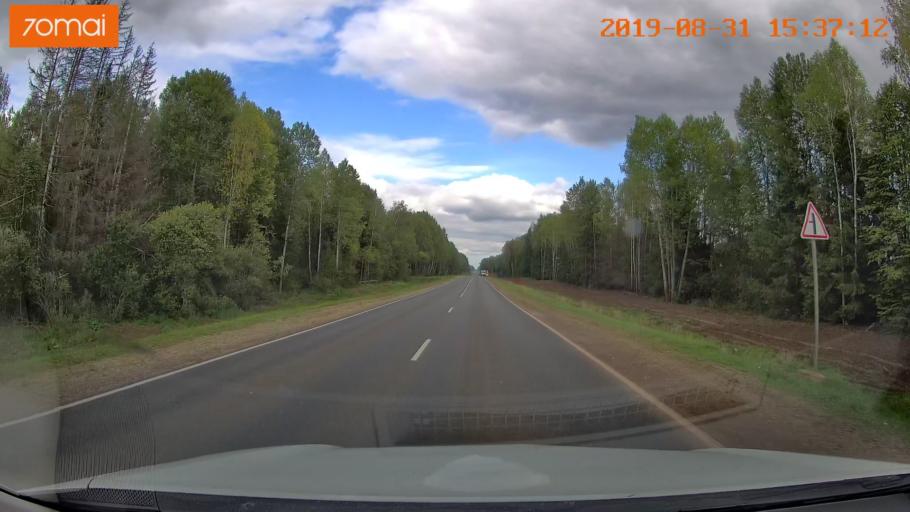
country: RU
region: Kaluga
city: Mosal'sk
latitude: 54.6166
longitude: 34.7783
